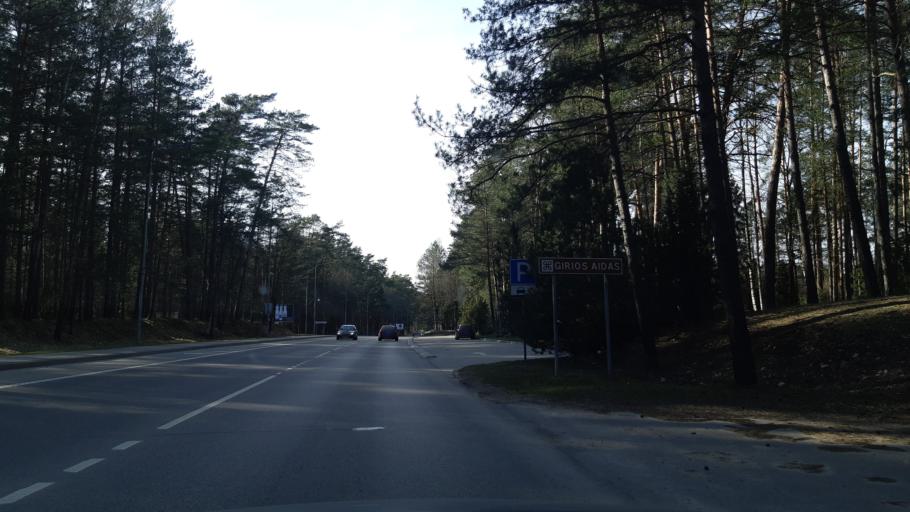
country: LT
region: Alytaus apskritis
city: Druskininkai
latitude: 54.0062
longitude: 24.0043
